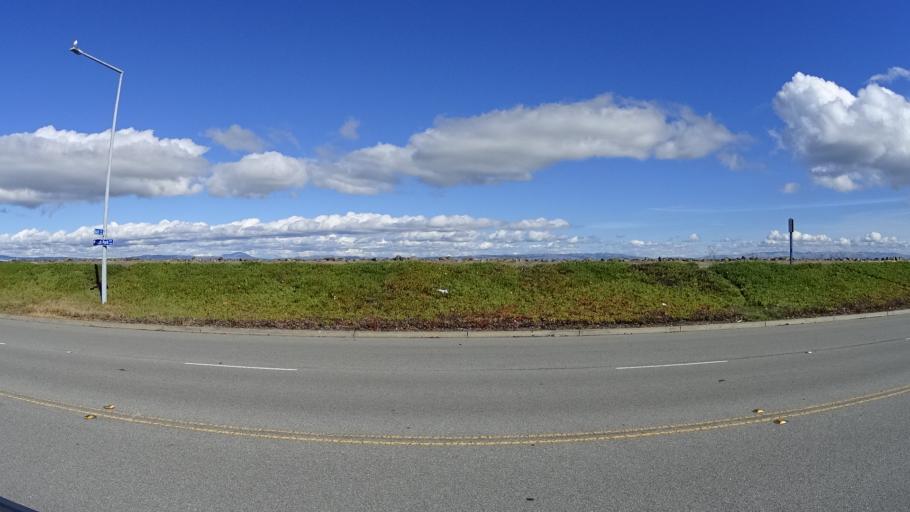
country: US
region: California
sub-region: San Mateo County
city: Foster City
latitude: 37.5657
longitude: -122.2511
